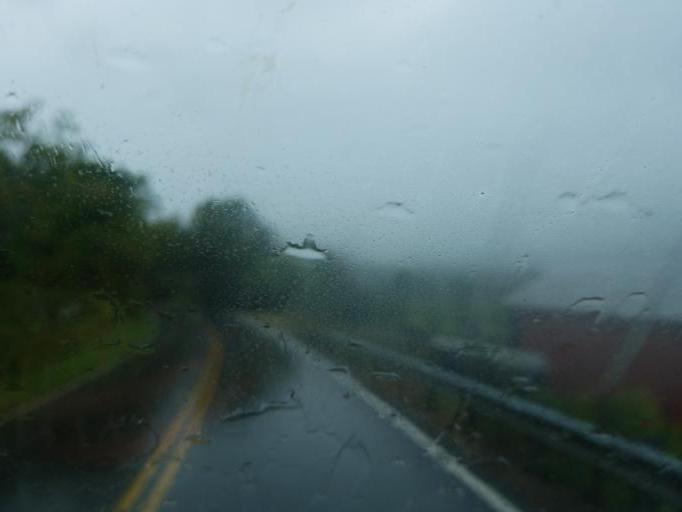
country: US
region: Kentucky
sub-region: Greenup County
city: Greenup
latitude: 38.4951
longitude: -82.9729
